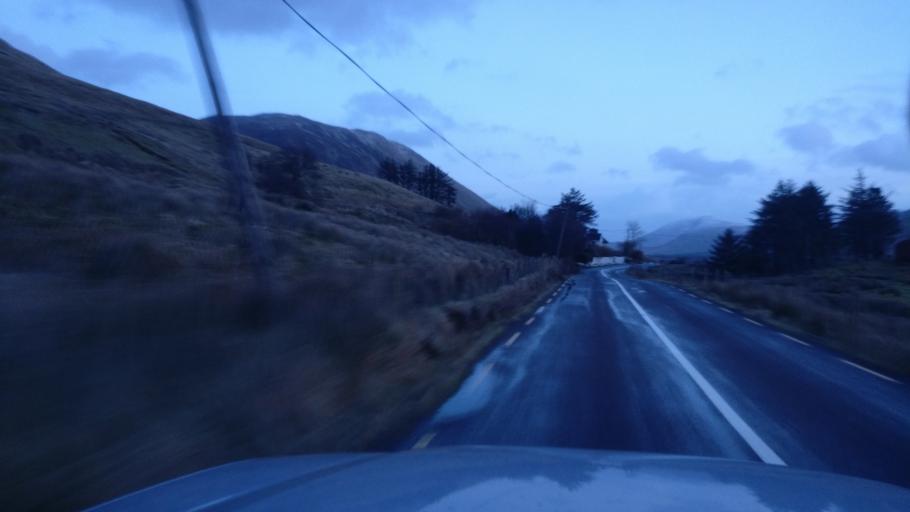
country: IE
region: Connaught
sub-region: Maigh Eo
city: Westport
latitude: 53.5777
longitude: -9.6664
